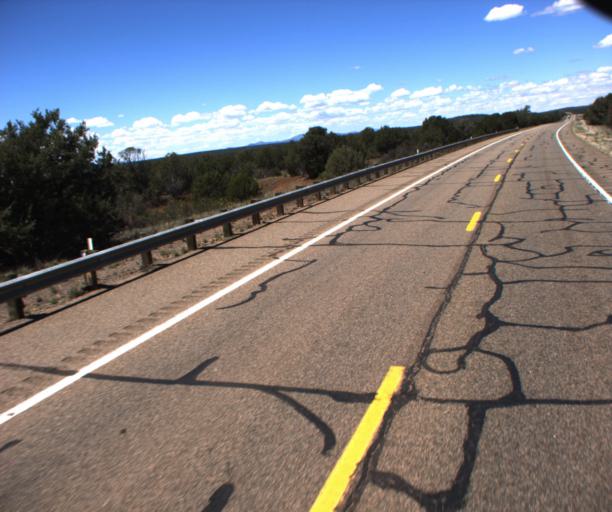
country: US
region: Arizona
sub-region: Yavapai County
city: Paulden
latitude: 35.1082
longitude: -112.4297
